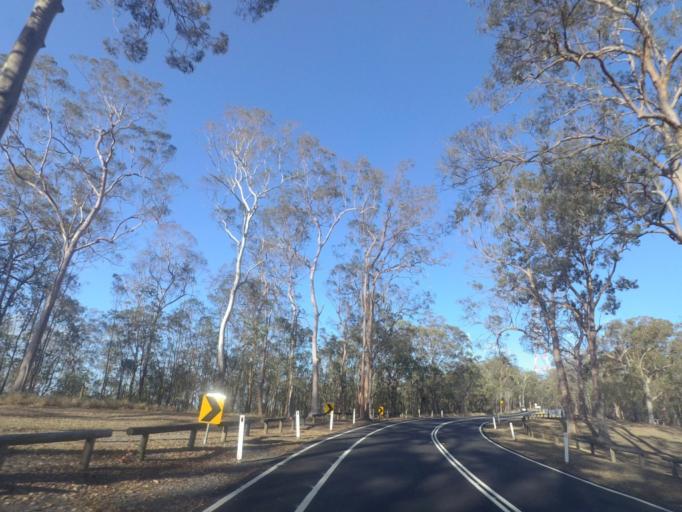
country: AU
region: Queensland
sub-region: Brisbane
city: Kenmore Hills
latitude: -27.4641
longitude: 152.9436
